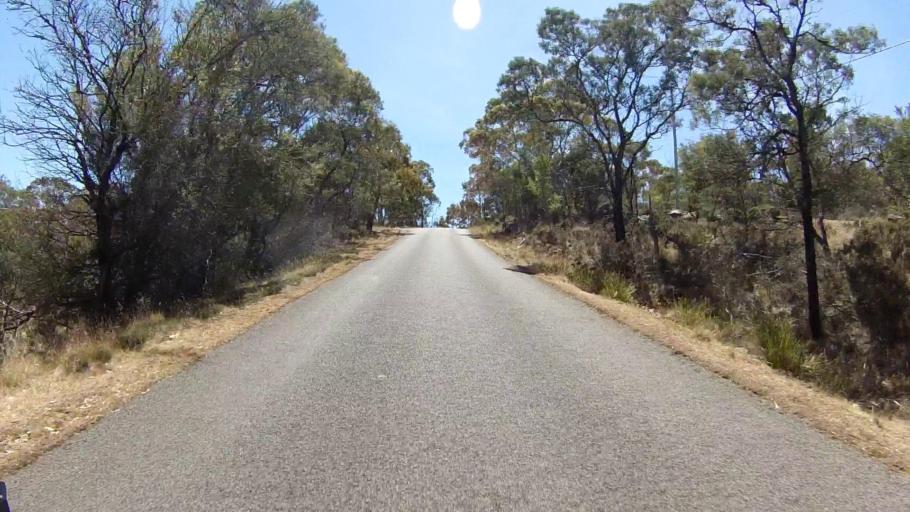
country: AU
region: Tasmania
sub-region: Clarence
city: Cambridge
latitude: -42.8491
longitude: 147.4308
